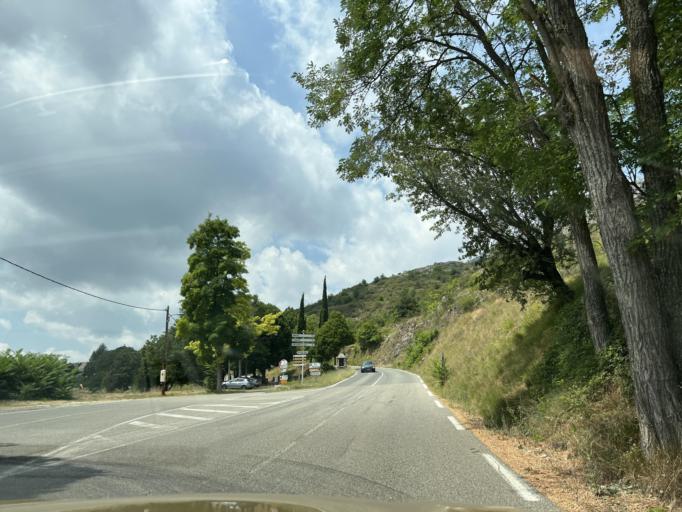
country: FR
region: Provence-Alpes-Cote d'Azur
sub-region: Departement des Alpes-Maritimes
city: Tourrettes-sur-Loup
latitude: 43.7967
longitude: 6.9503
